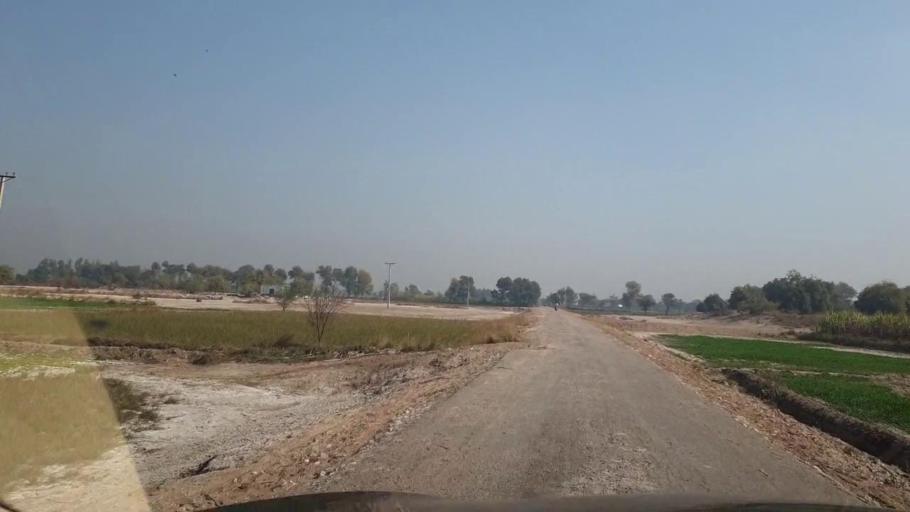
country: PK
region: Sindh
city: Ubauro
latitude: 28.1304
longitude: 69.7553
